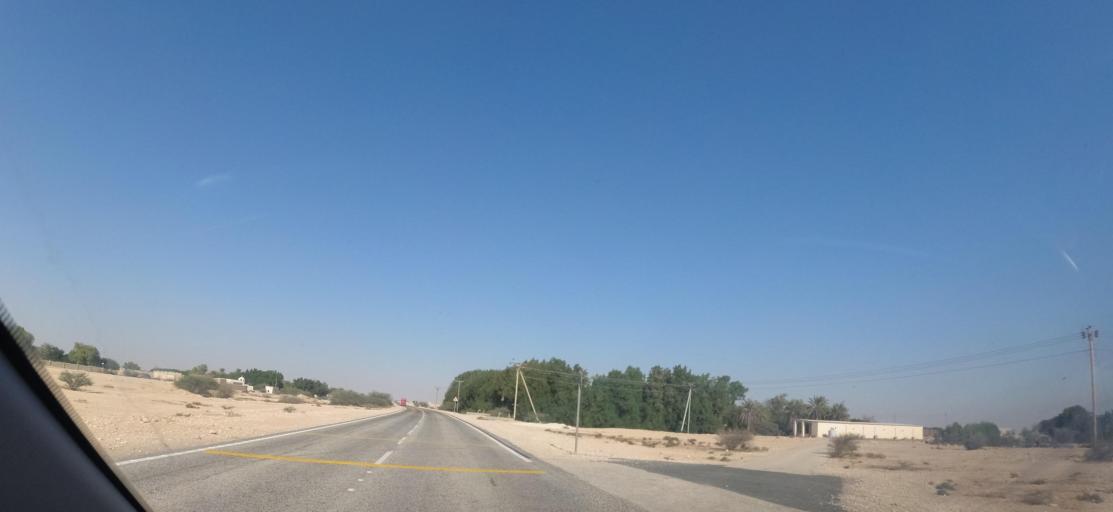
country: QA
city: Al Jumayliyah
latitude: 25.6251
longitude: 51.0908
